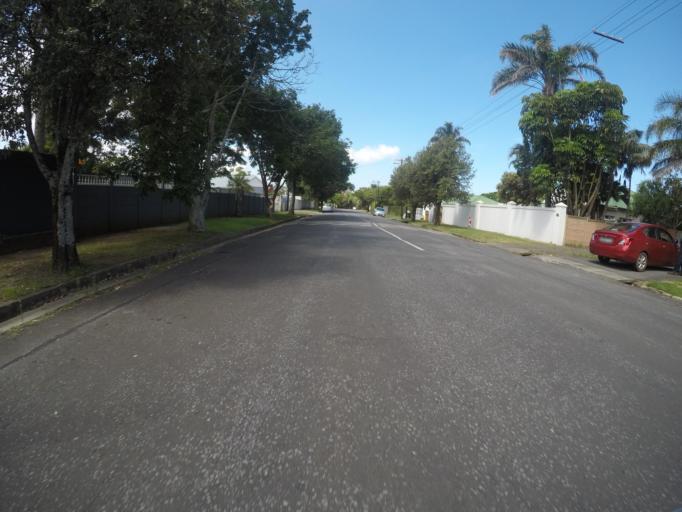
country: ZA
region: Eastern Cape
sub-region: Buffalo City Metropolitan Municipality
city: East London
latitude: -32.9759
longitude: 27.9044
